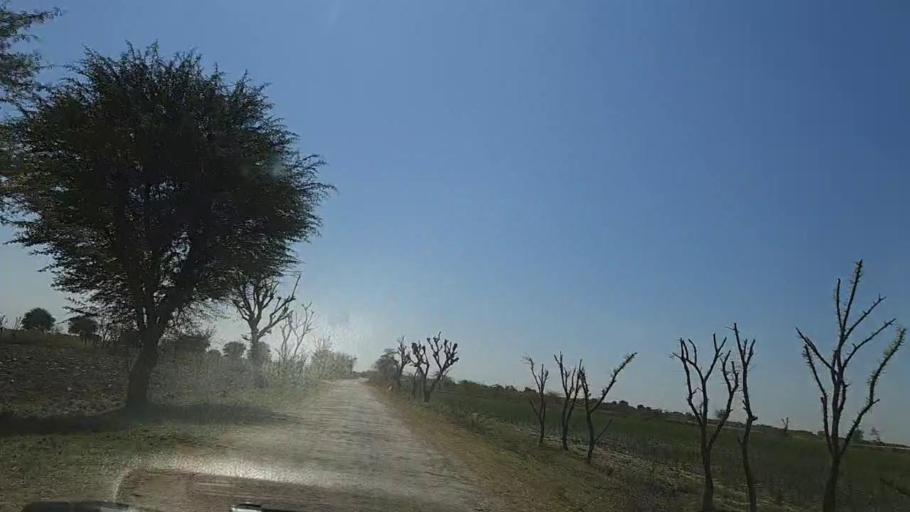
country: PK
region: Sindh
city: Dhoro Naro
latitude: 25.4871
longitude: 69.5434
